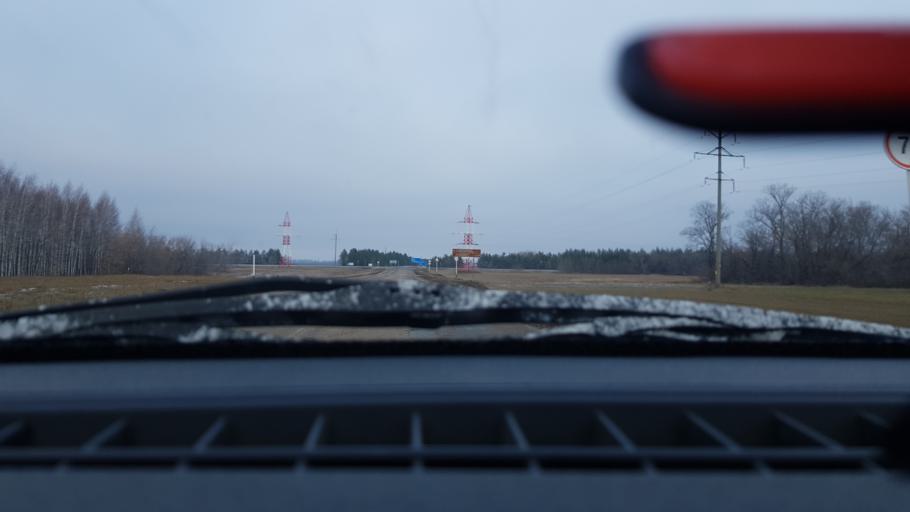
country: RU
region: Tatarstan
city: Kuybyshevskiy Zaton
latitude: 54.9436
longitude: 49.4521
